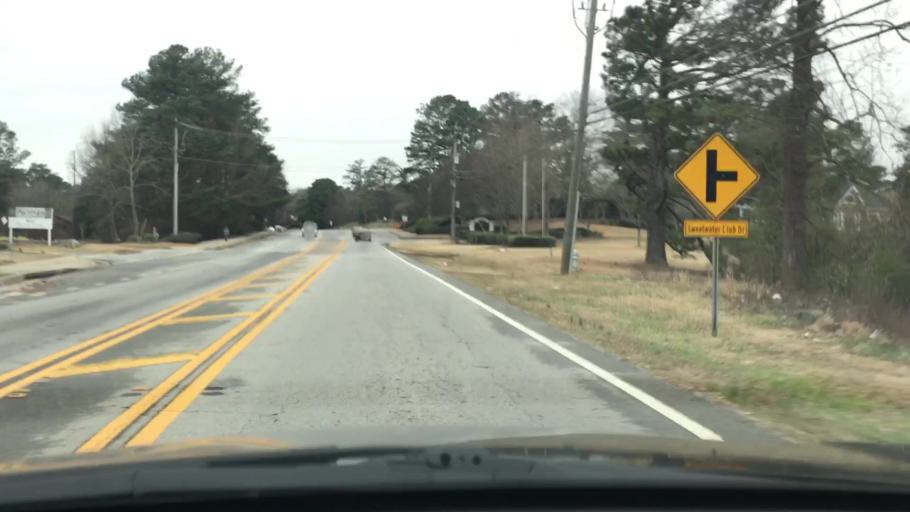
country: US
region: Georgia
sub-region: Gwinnett County
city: Lilburn
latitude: 33.9425
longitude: -84.1145
